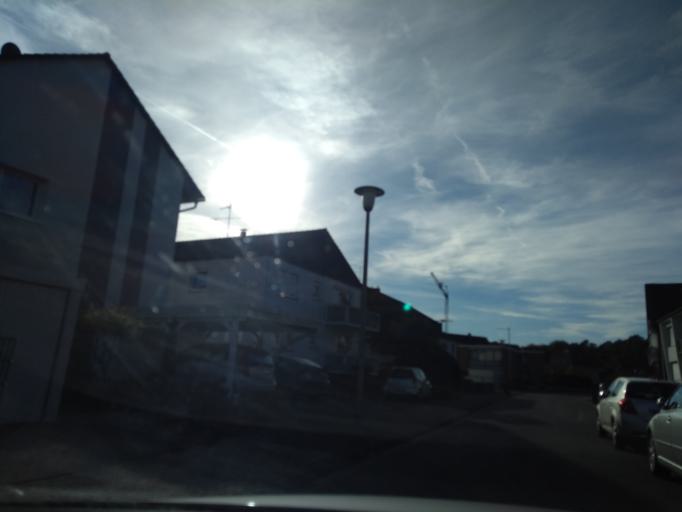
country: DE
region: North Rhine-Westphalia
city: Bad Lippspringe
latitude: 51.7895
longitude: 8.8236
